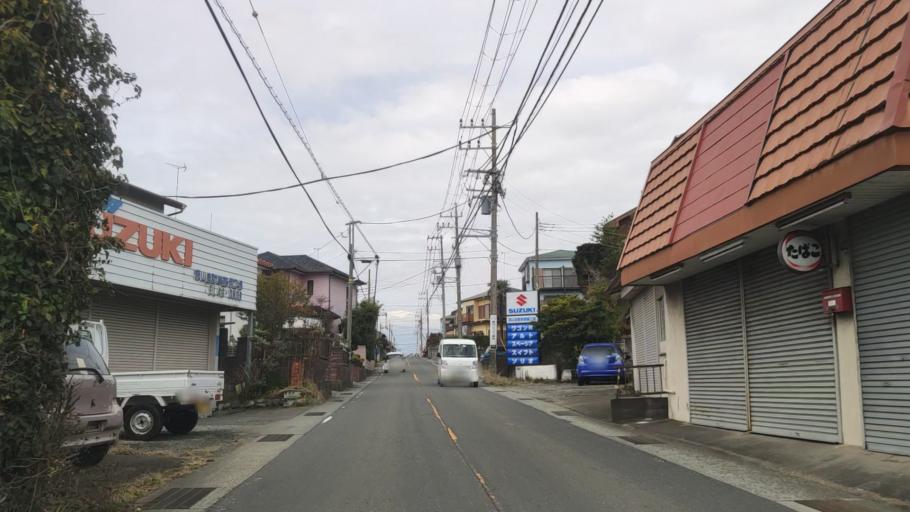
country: JP
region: Kanagawa
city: Ninomiya
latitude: 35.2933
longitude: 139.2338
